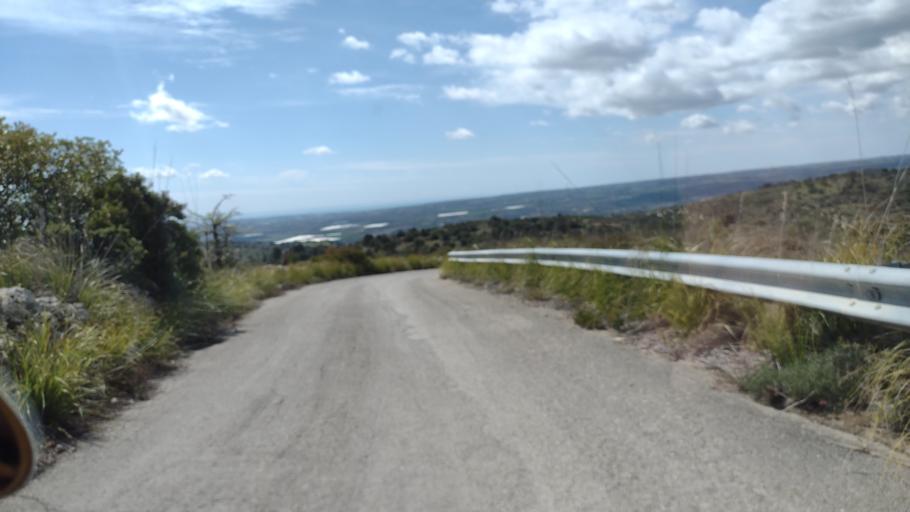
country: IT
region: Sicily
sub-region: Provincia di Siracusa
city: Rosolini
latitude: 36.9111
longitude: 14.9791
